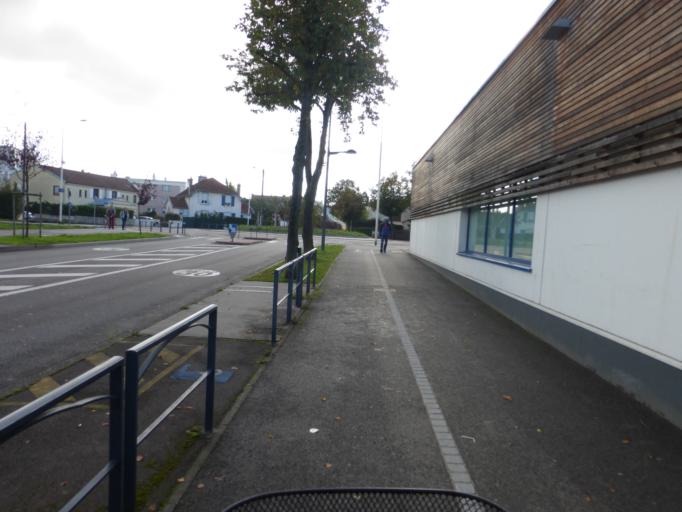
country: FR
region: Lorraine
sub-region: Departement de Meurthe-et-Moselle
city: Villers-les-Nancy
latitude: 48.6695
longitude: 6.1633
